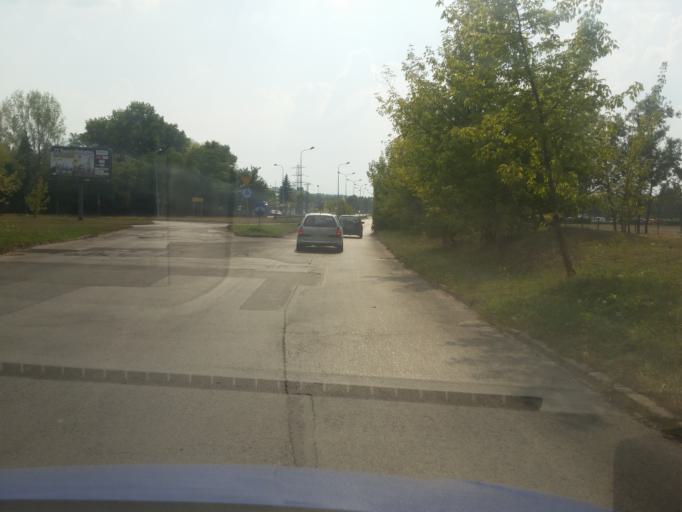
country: PL
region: Silesian Voivodeship
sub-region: Sosnowiec
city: Sosnowiec
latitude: 50.2588
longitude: 19.1362
